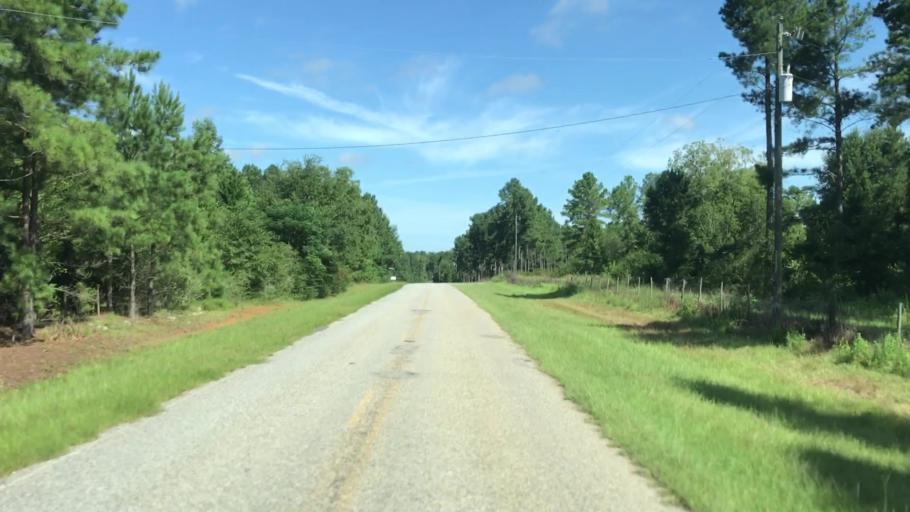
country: US
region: Georgia
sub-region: Jefferson County
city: Wadley
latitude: 32.8074
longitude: -82.3717
